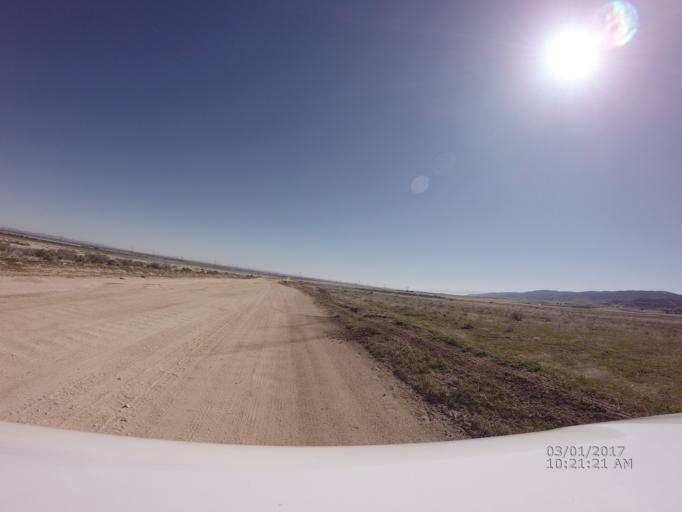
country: US
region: California
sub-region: Los Angeles County
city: Green Valley
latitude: 34.6891
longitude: -118.3519
